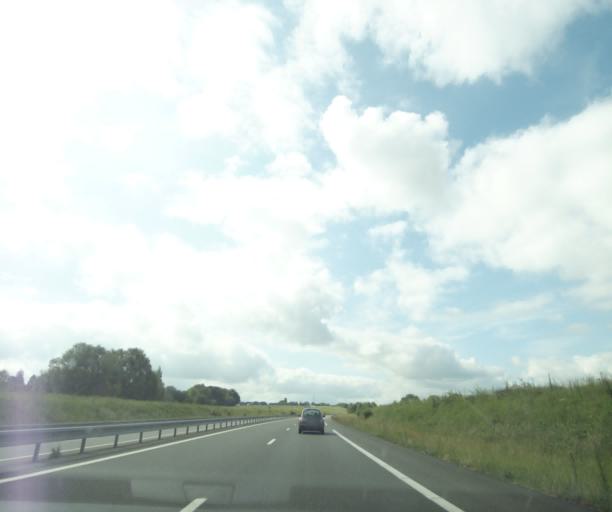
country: FR
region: Pays de la Loire
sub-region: Departement de Maine-et-Loire
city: Saint-Philbert-du-Peuple
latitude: 47.3787
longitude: -0.0861
